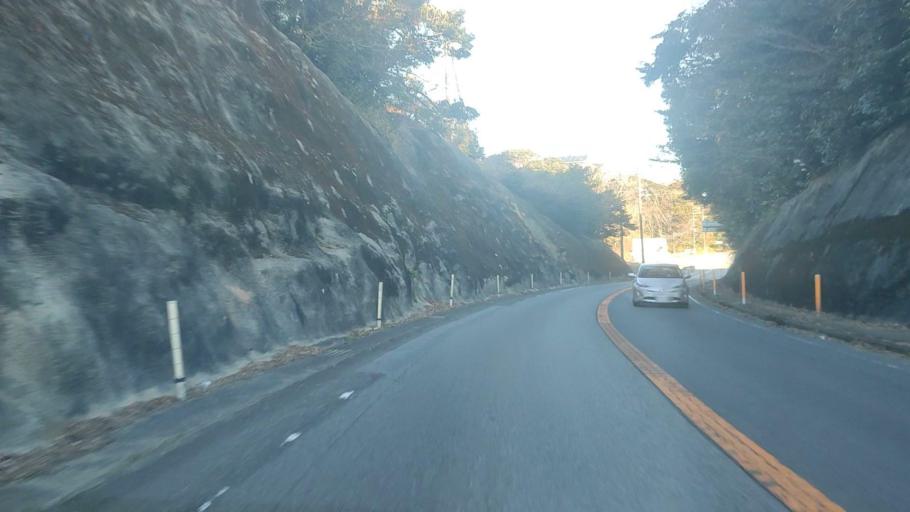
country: JP
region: Miyazaki
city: Nobeoka
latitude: 32.3476
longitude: 131.6225
